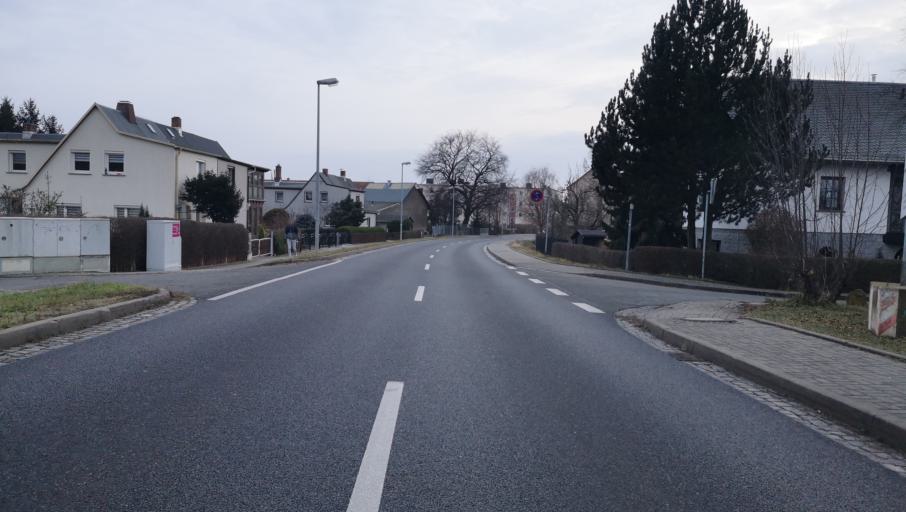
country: DE
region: Thuringia
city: Ronneburg
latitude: 50.8692
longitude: 12.1863
